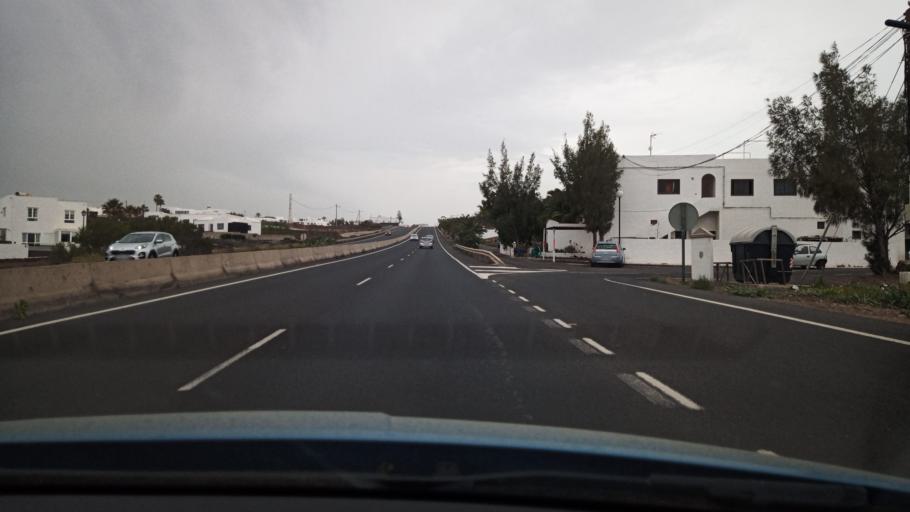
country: ES
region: Canary Islands
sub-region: Provincia de Las Palmas
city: Tias
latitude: 28.9568
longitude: -13.6391
